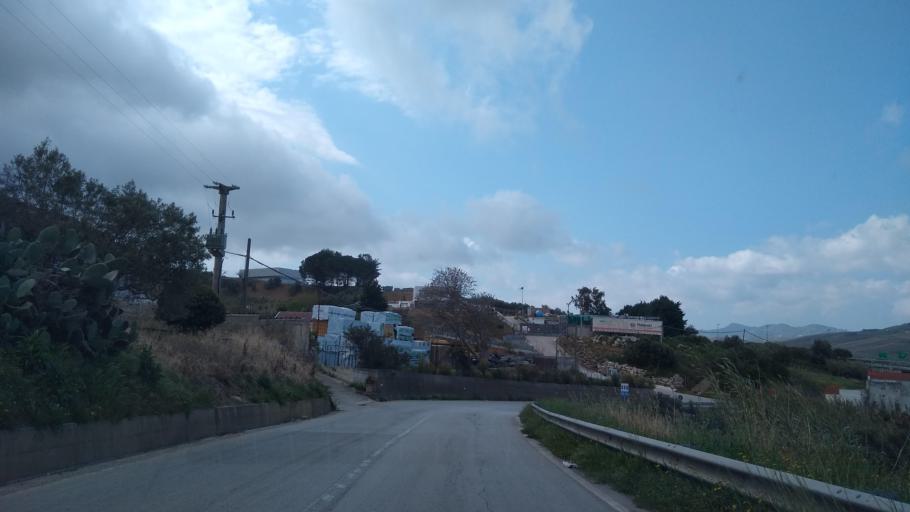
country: IT
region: Sicily
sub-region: Trapani
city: Alcamo
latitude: 37.9706
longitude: 12.9234
